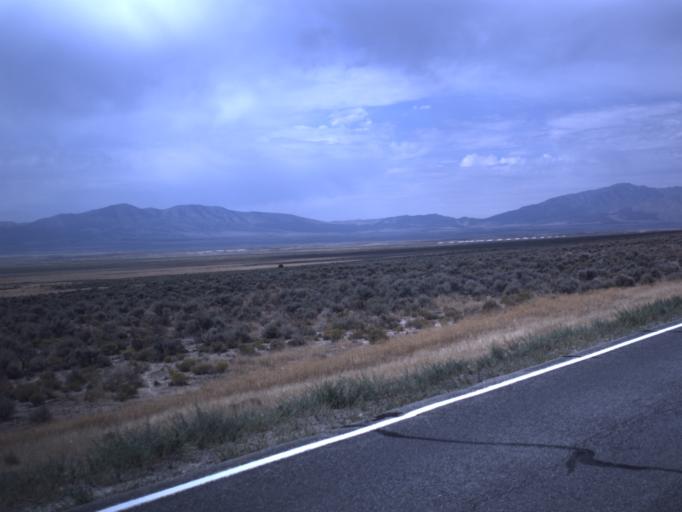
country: US
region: Utah
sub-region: Utah County
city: Eagle Mountain
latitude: 40.2728
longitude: -112.2472
